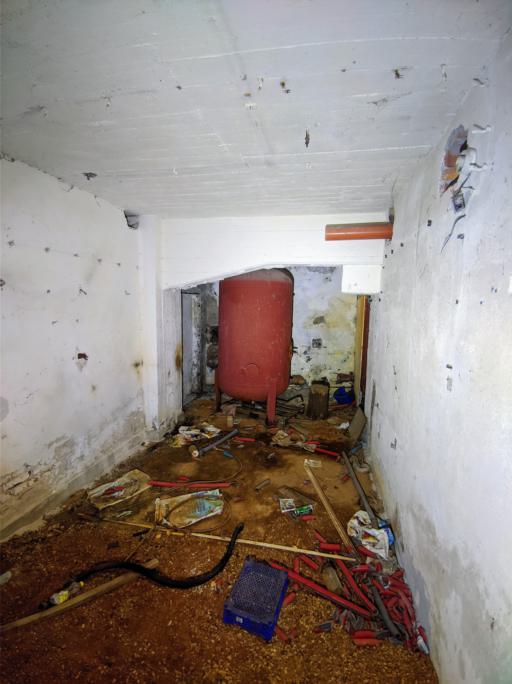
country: DE
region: Brandenburg
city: Forst
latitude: 51.7429
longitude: 14.6638
